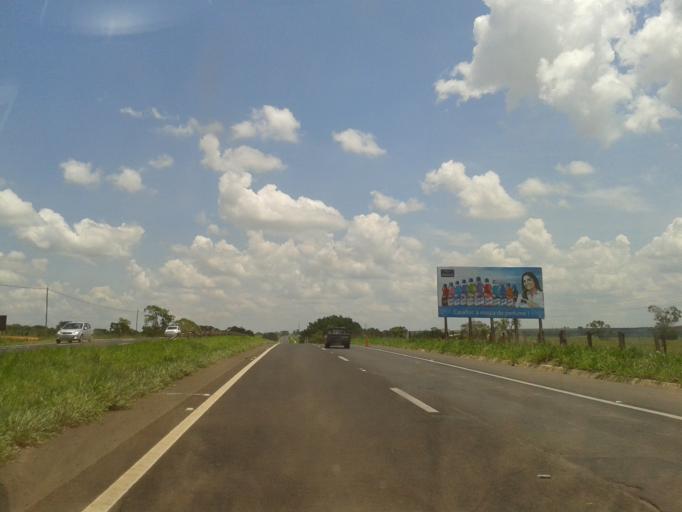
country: BR
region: Minas Gerais
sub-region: Uberlandia
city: Uberlandia
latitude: -18.8704
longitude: -48.5524
